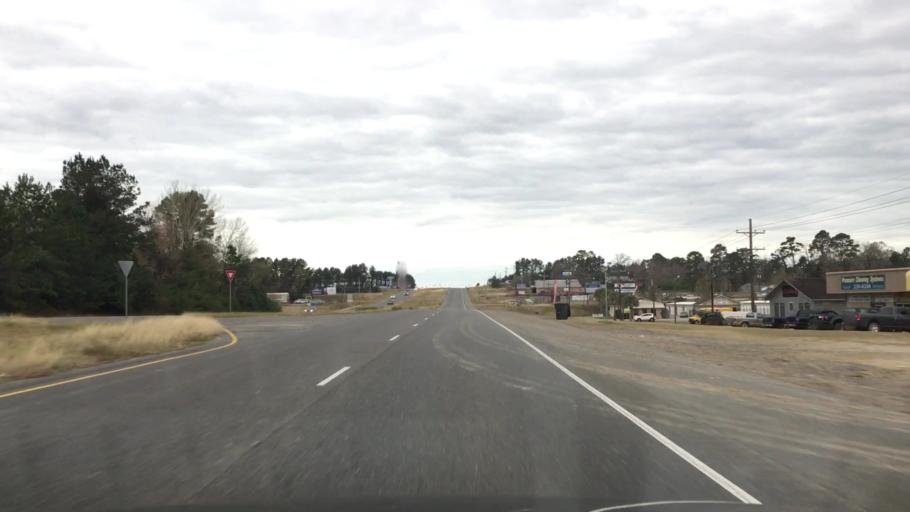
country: US
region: Louisiana
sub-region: Vernon Parish
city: New Llano
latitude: 31.0948
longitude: -93.2701
